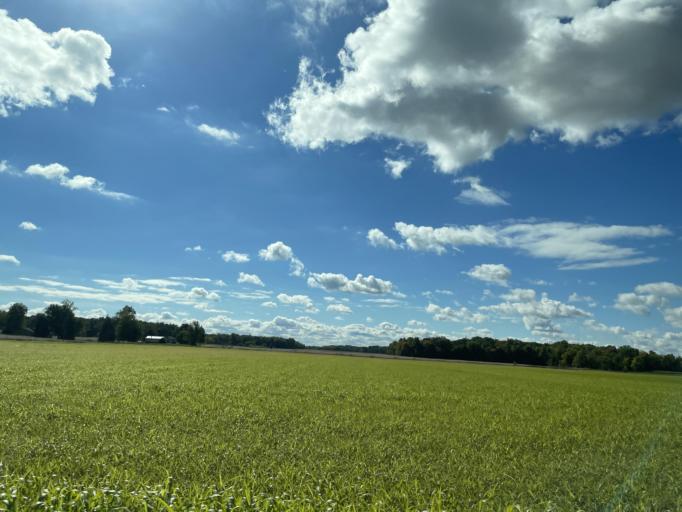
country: US
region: Indiana
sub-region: Allen County
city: Fort Wayne
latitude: 41.1182
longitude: -85.2471
